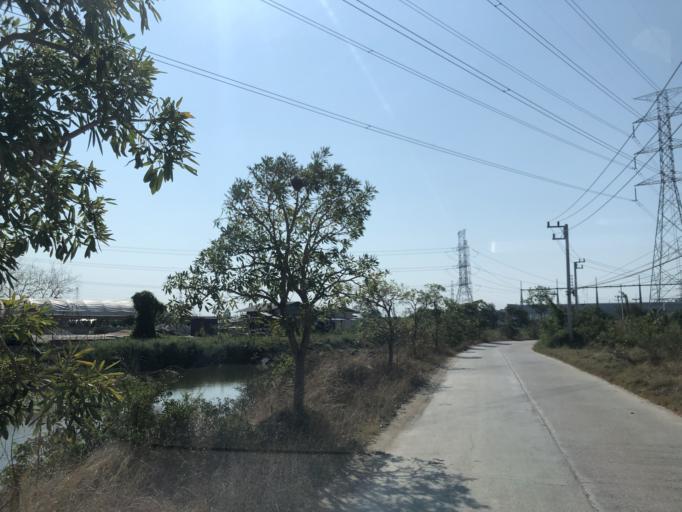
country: TH
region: Chachoengsao
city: Bang Pakong
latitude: 13.5135
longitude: 101.0244
